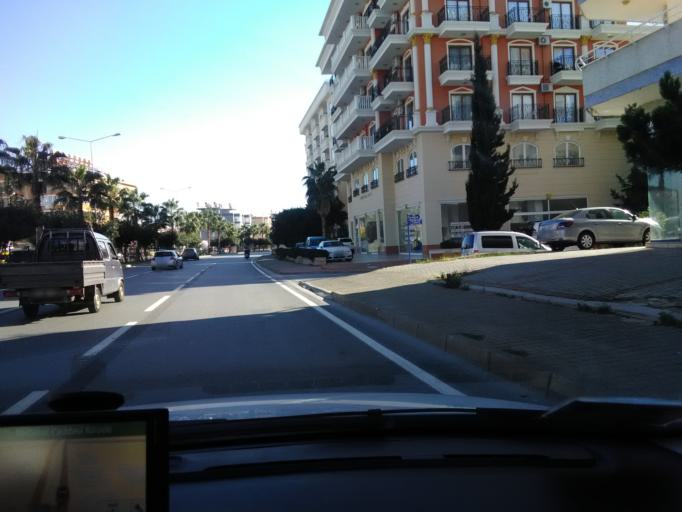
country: TR
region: Antalya
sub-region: Alanya
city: Alanya
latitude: 36.5368
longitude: 32.0426
